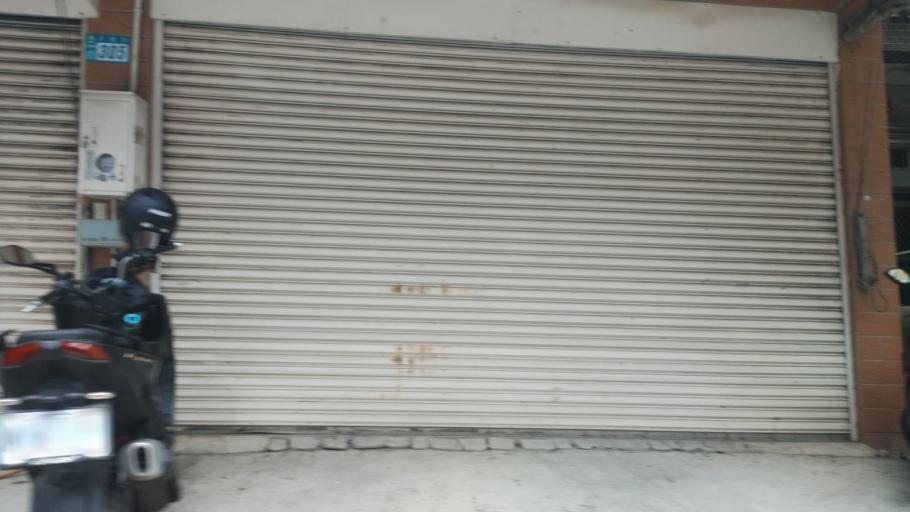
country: TW
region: Taipei
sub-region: Taipei
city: Banqiao
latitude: 24.9236
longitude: 121.4291
